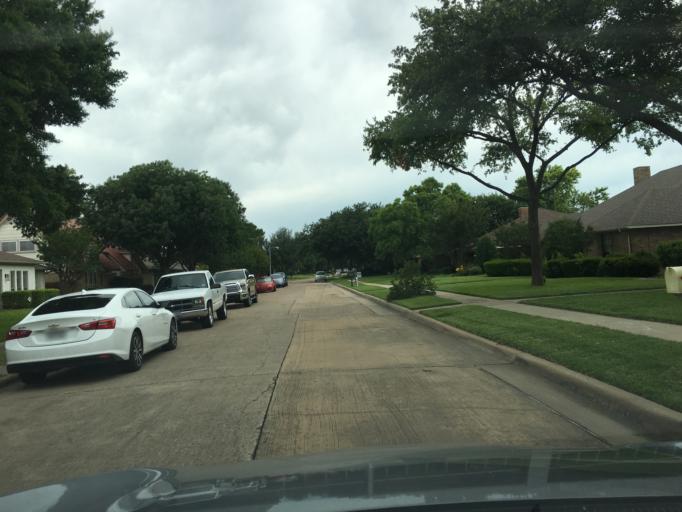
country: US
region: Texas
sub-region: Dallas County
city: Richardson
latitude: 32.9439
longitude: -96.7070
